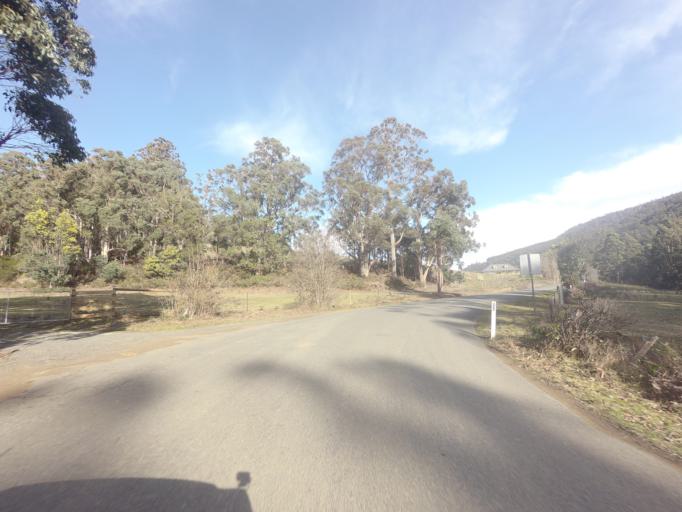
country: AU
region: Tasmania
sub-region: Huon Valley
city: Huonville
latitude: -43.0497
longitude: 147.1109
